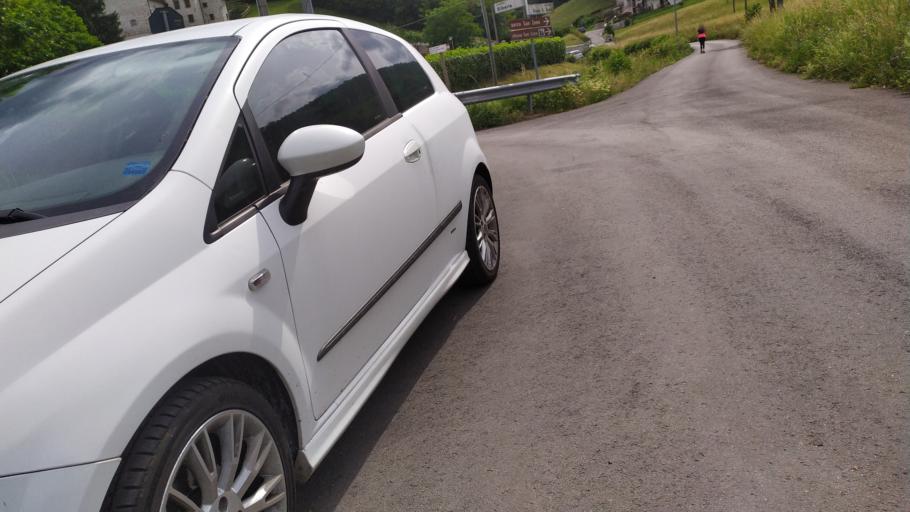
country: IT
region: Veneto
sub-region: Provincia di Vicenza
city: Schio
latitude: 45.6973
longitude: 11.3366
